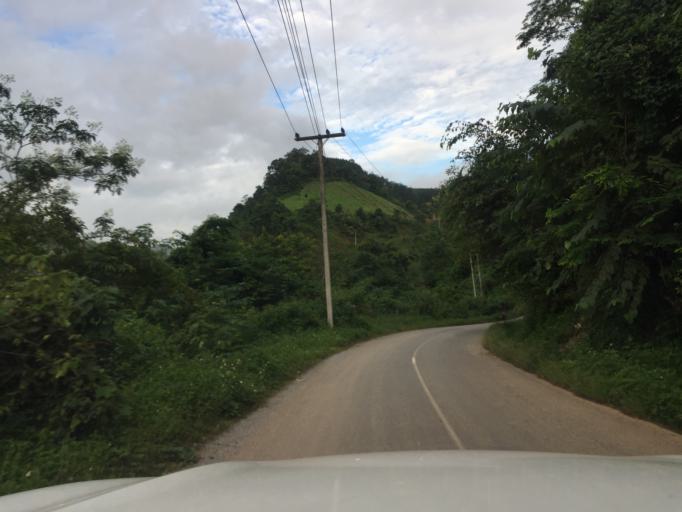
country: LA
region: Phongsali
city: Khoa
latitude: 21.1042
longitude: 102.2994
